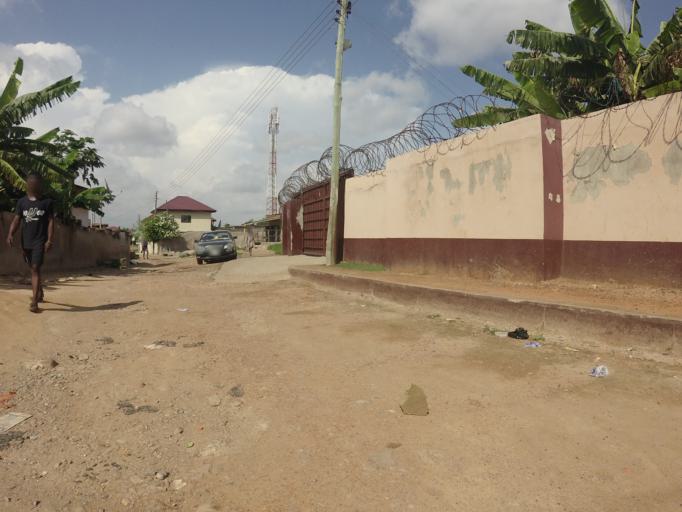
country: GH
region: Greater Accra
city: Dome
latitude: 5.6165
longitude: -0.2411
